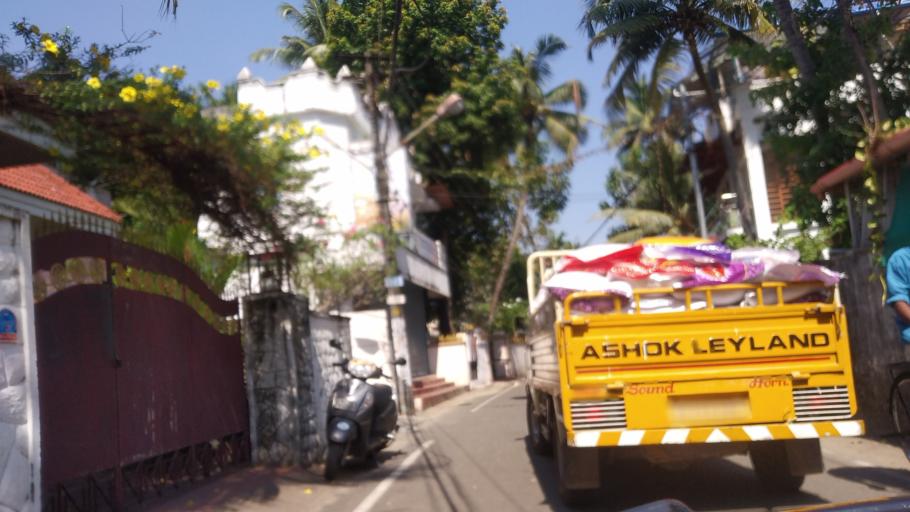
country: IN
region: Kerala
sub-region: Ernakulam
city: Cochin
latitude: 9.9381
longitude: 76.2486
